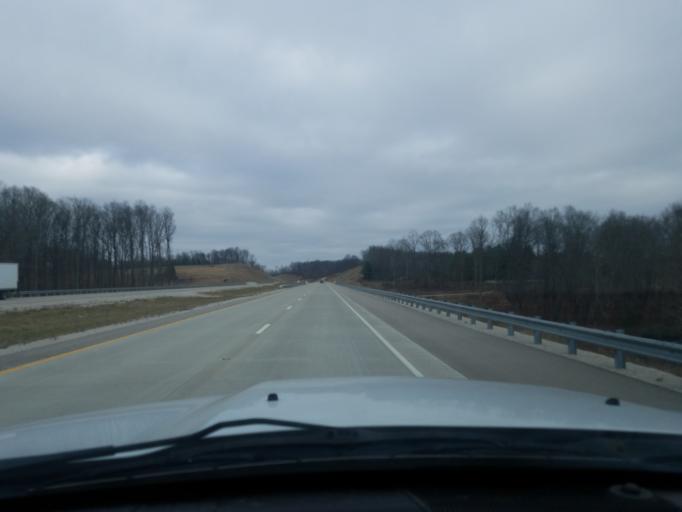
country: US
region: Indiana
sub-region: Monroe County
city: Bloomington
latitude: 39.0747
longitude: -86.5945
